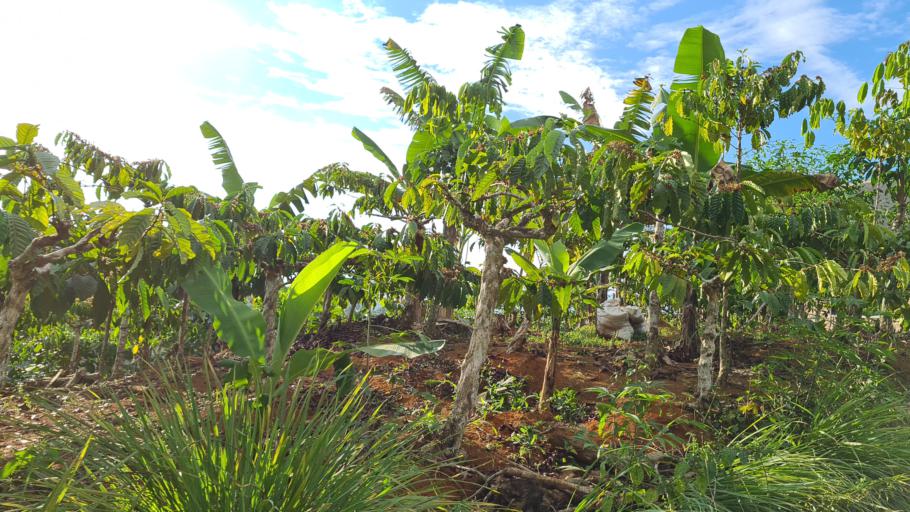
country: ID
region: Lampung
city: Kenali
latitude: -5.0970
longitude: 104.3968
